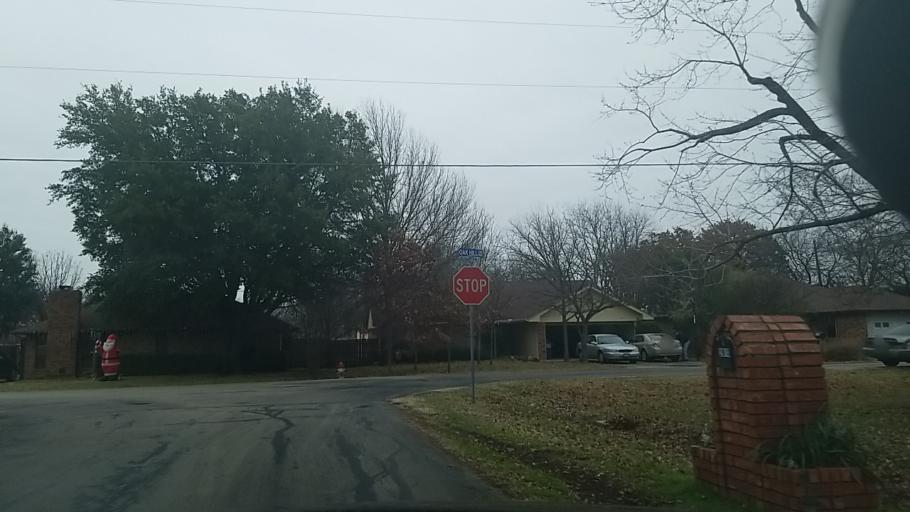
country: US
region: Texas
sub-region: Denton County
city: Corinth
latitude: 33.1473
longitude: -97.0667
